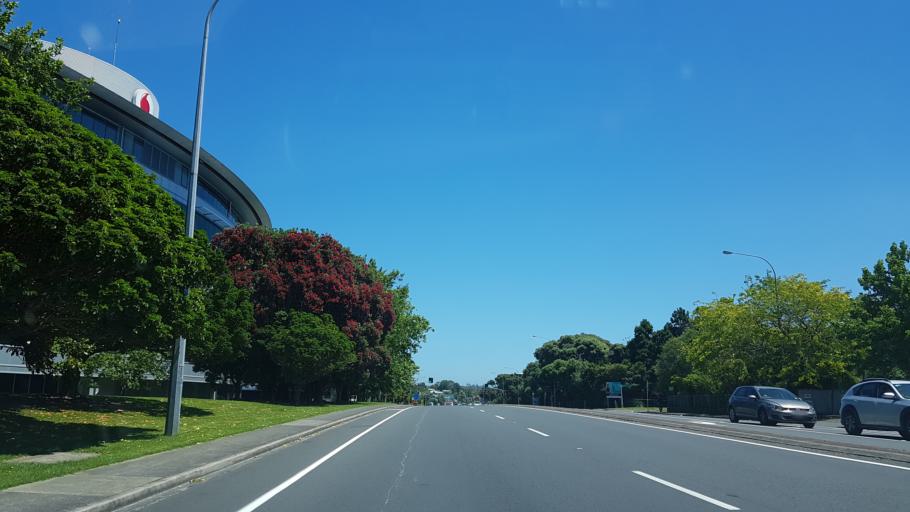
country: NZ
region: Auckland
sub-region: Auckland
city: North Shore
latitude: -36.7853
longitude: 174.7560
